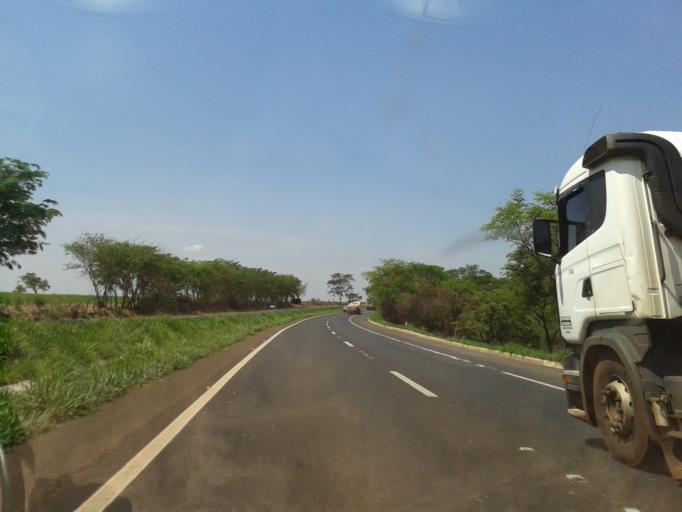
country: BR
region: Minas Gerais
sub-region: Monte Alegre De Minas
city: Monte Alegre de Minas
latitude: -18.8688
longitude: -48.5959
